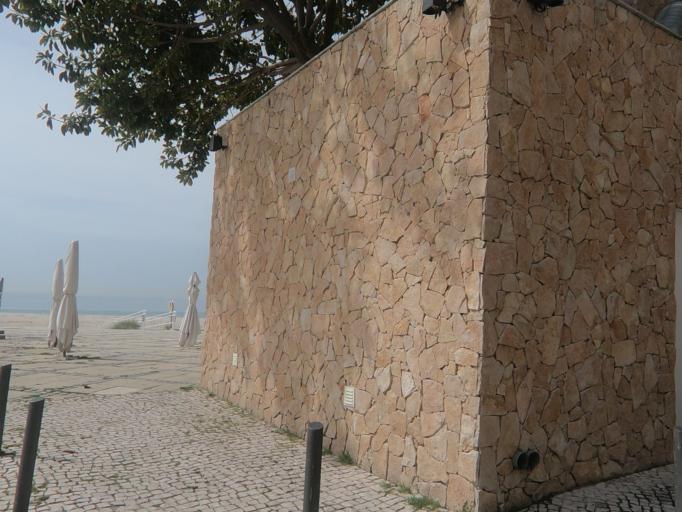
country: PT
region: Setubal
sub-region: Setubal
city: Setubal
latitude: 38.4849
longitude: -8.9445
